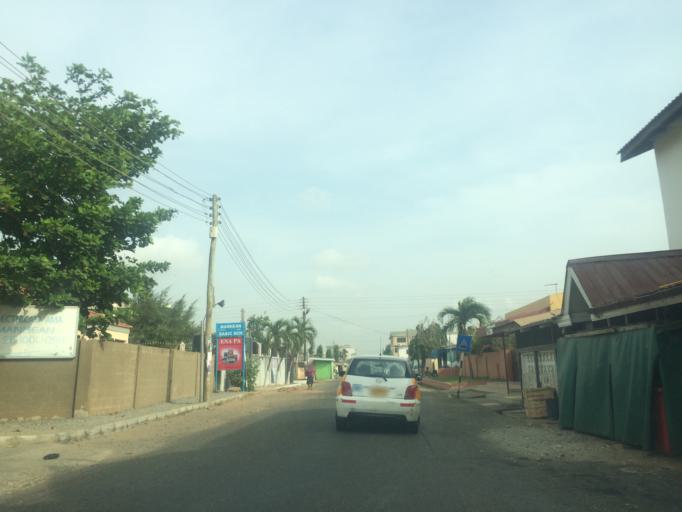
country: GH
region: Greater Accra
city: Accra
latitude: 5.5545
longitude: -0.1754
